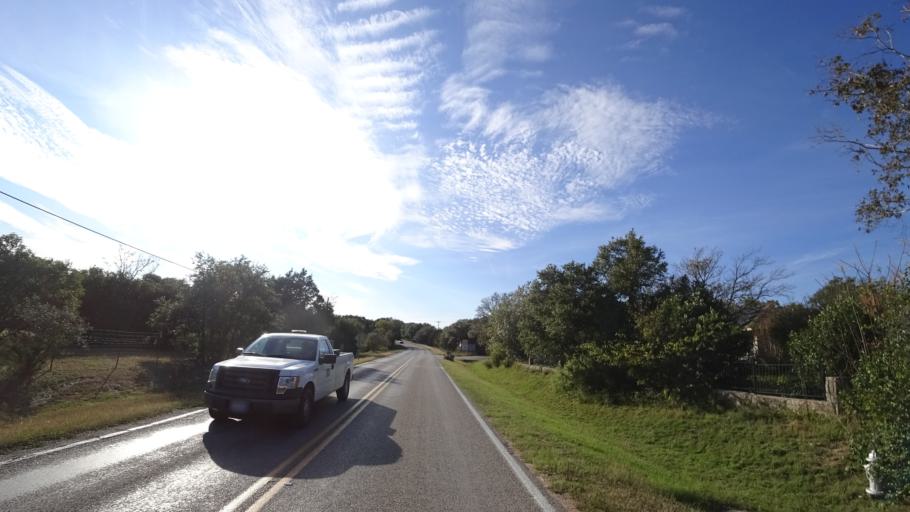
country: US
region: Texas
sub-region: Travis County
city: Bee Cave
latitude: 30.2469
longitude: -97.9293
